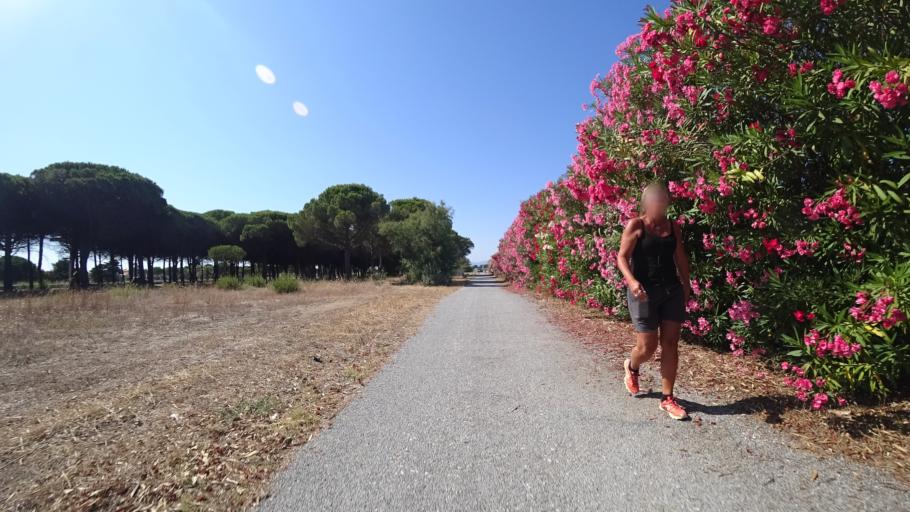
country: FR
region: Languedoc-Roussillon
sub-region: Departement des Pyrenees-Orientales
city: Le Barcares
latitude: 42.8109
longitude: 3.0302
